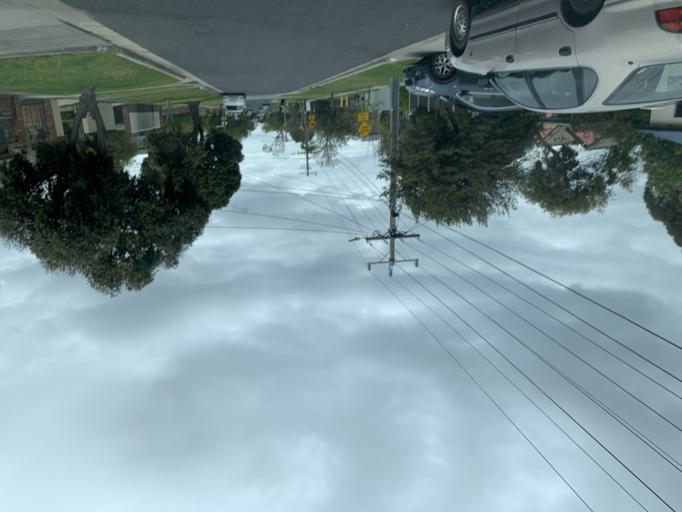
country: AU
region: Victoria
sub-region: Kingston
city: Parkdale
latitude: -37.9873
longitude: 145.0755
